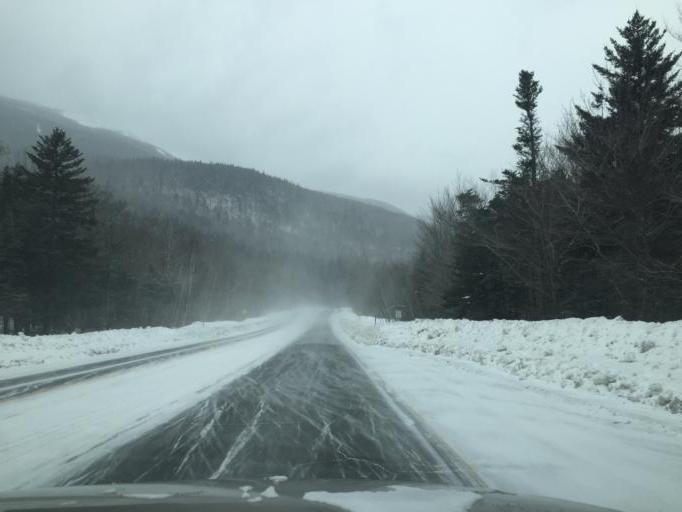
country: US
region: New Hampshire
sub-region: Coos County
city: Gorham
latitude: 44.2304
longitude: -71.2539
